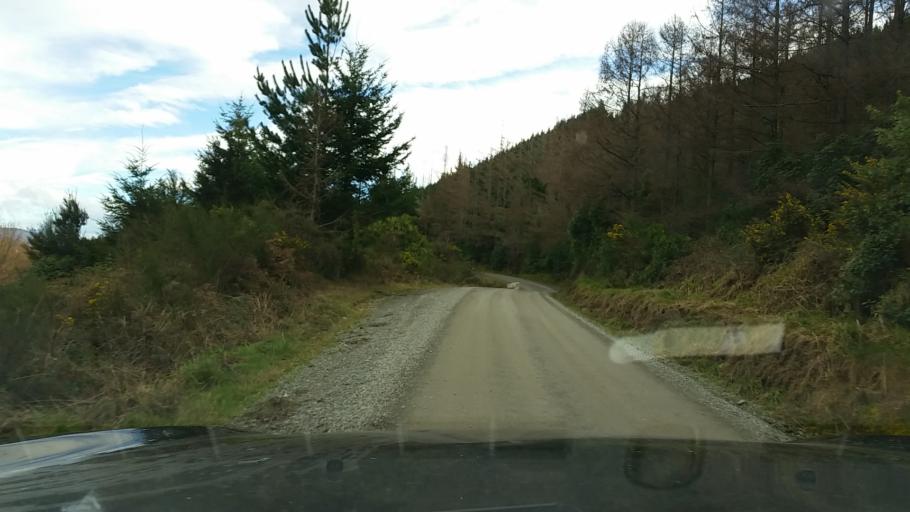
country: NZ
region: Nelson
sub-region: Nelson City
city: Nelson
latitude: -41.5774
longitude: 173.4337
